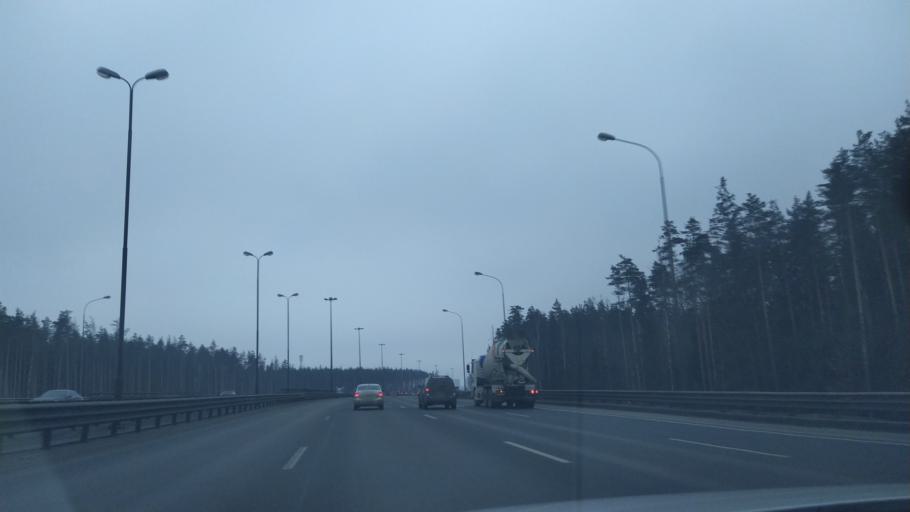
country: RU
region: Leningrad
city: Yanino Vtoroye
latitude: 59.9655
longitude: 30.5534
